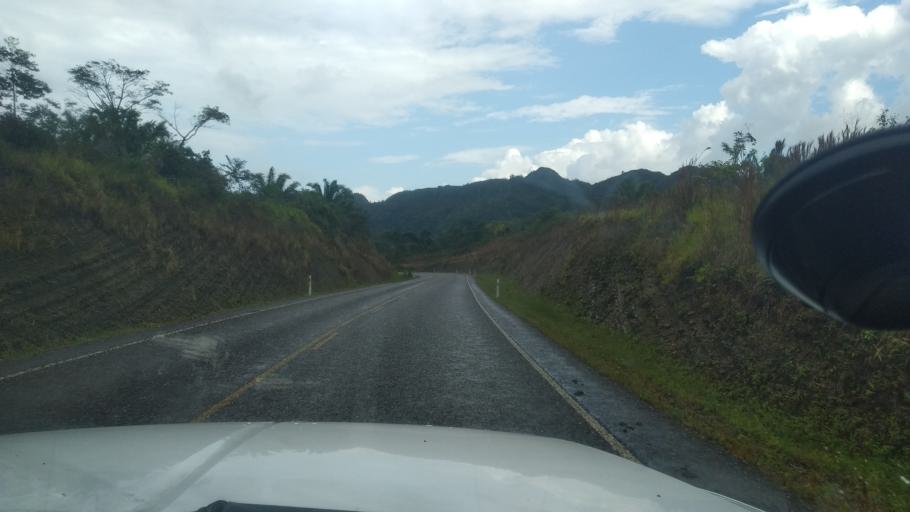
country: GT
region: Peten
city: San Luis
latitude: 16.1838
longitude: -89.2019
